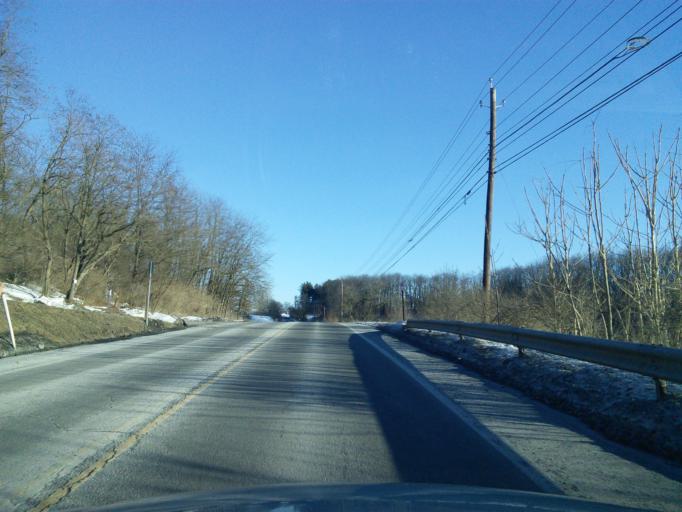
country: US
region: Pennsylvania
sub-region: Centre County
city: State College
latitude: 40.8208
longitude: -77.8632
